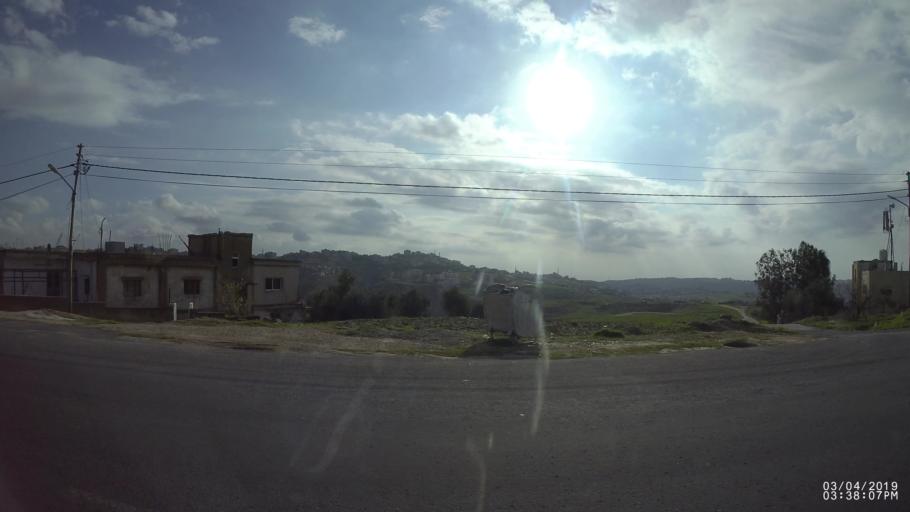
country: JO
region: Amman
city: Umm as Summaq
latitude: 31.9234
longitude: 35.8481
